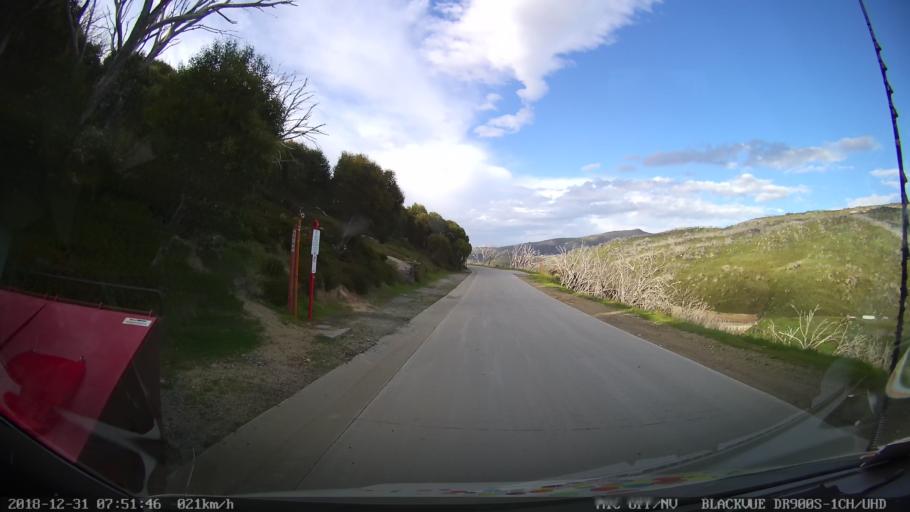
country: AU
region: New South Wales
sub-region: Snowy River
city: Jindabyne
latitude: -36.3780
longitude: 148.3749
